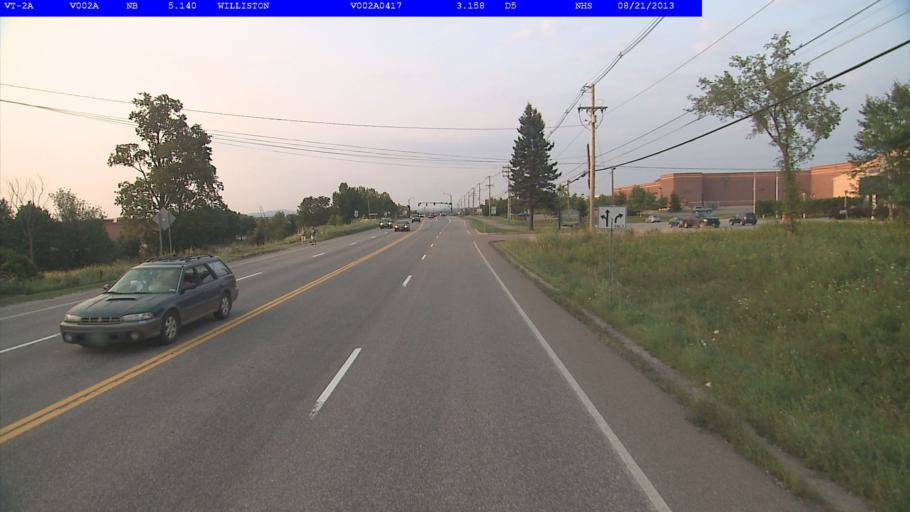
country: US
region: Vermont
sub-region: Chittenden County
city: Williston
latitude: 44.4418
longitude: -73.1136
